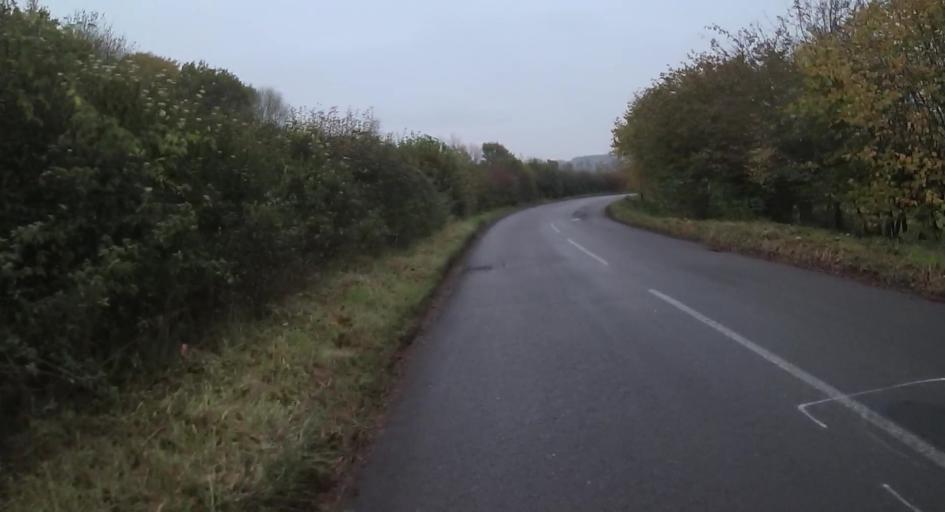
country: GB
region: England
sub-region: Hampshire
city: Kingsley
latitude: 51.1640
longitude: -0.8703
